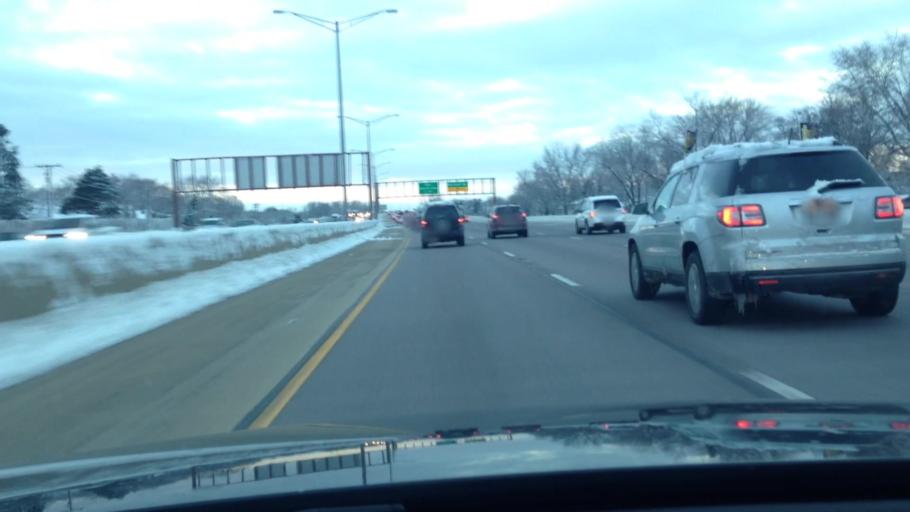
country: US
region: Illinois
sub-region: Cook County
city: Rolling Meadows
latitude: 42.0766
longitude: -88.0284
